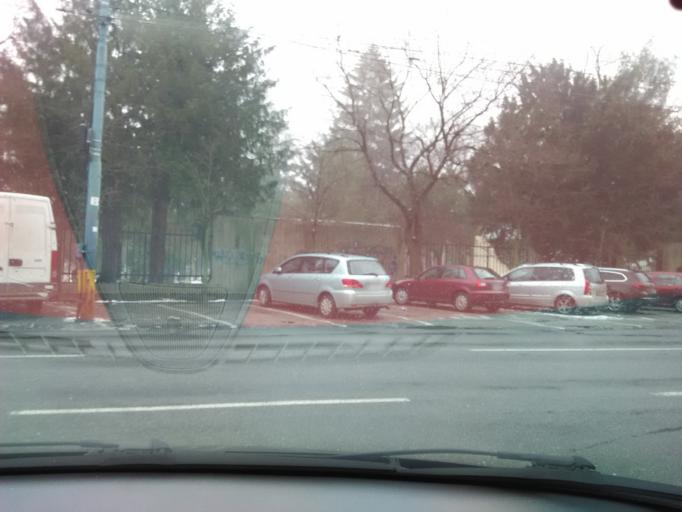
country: SK
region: Bratislavsky
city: Bratislava
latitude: 48.1472
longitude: 17.1215
